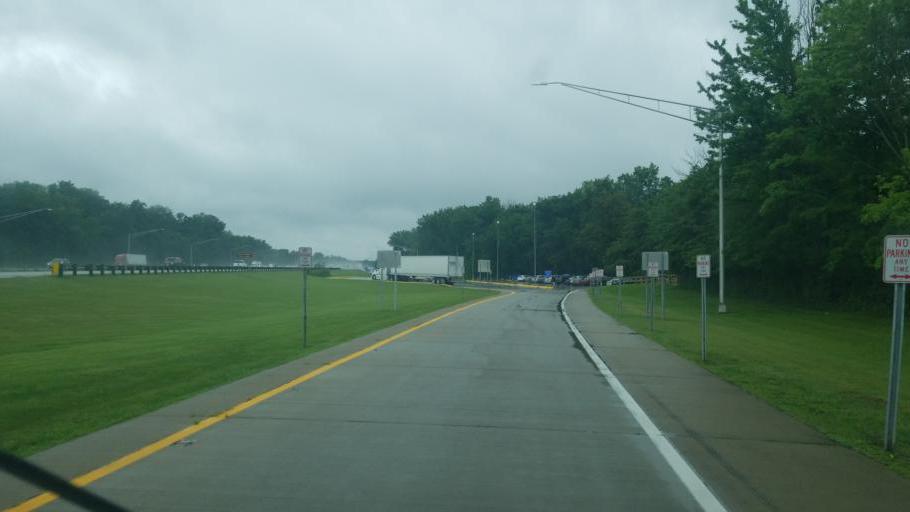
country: US
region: Ohio
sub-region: Delaware County
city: Sunbury
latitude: 40.2281
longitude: -82.9295
